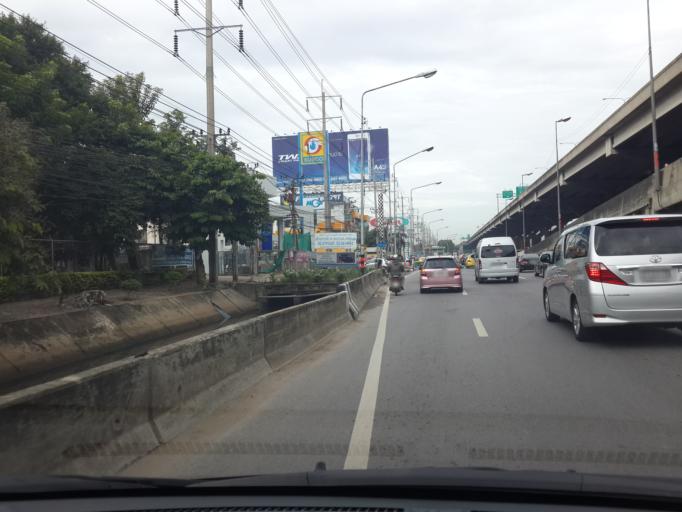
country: TH
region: Bangkok
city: Lak Si
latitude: 13.8596
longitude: 100.5683
